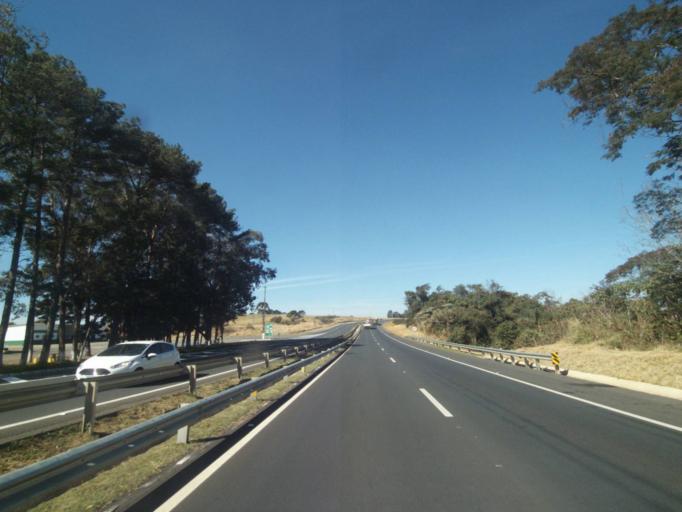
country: BR
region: Parana
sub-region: Tibagi
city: Tibagi
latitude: -24.8227
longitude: -50.4815
